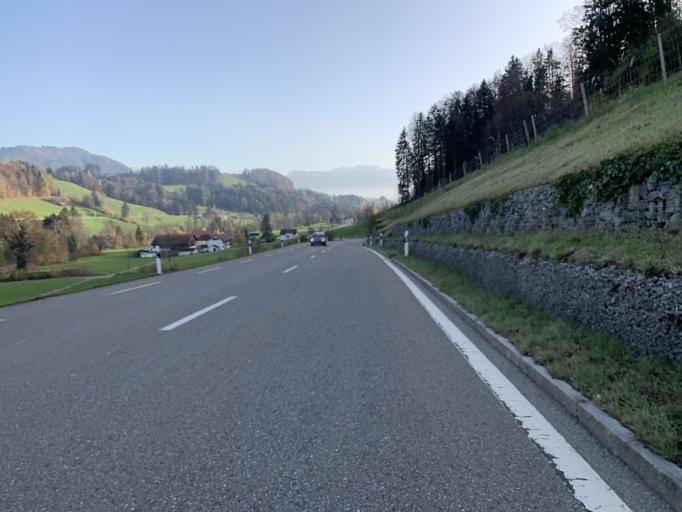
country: CH
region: Zurich
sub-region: Bezirk Hinwil
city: Wald
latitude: 47.3028
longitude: 8.9138
